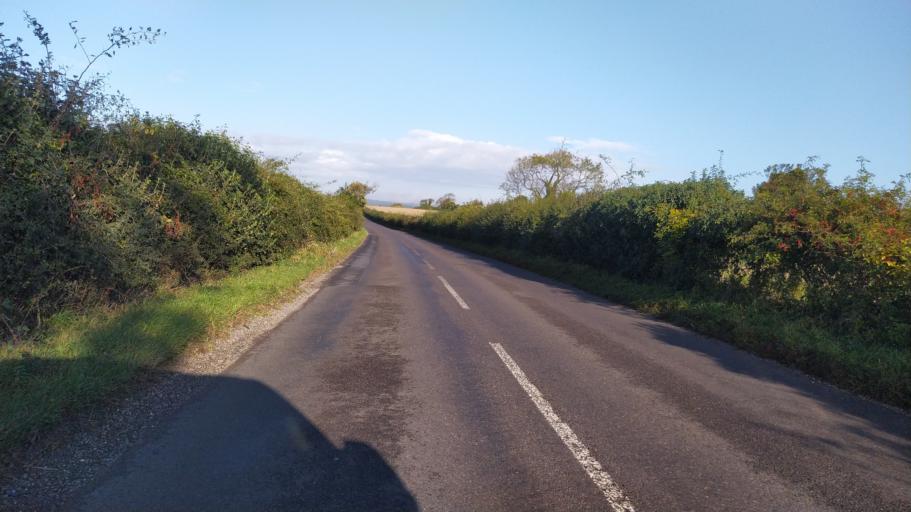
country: GB
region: England
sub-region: Wiltshire
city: Bower Chalke
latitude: 50.9056
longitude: -2.0348
